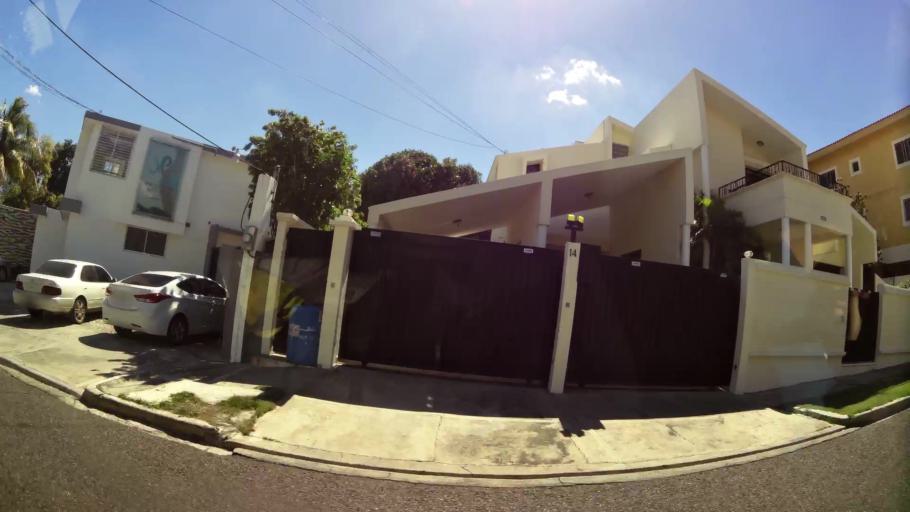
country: DO
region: Santiago
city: Santiago de los Caballeros
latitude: 19.4484
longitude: -70.6923
